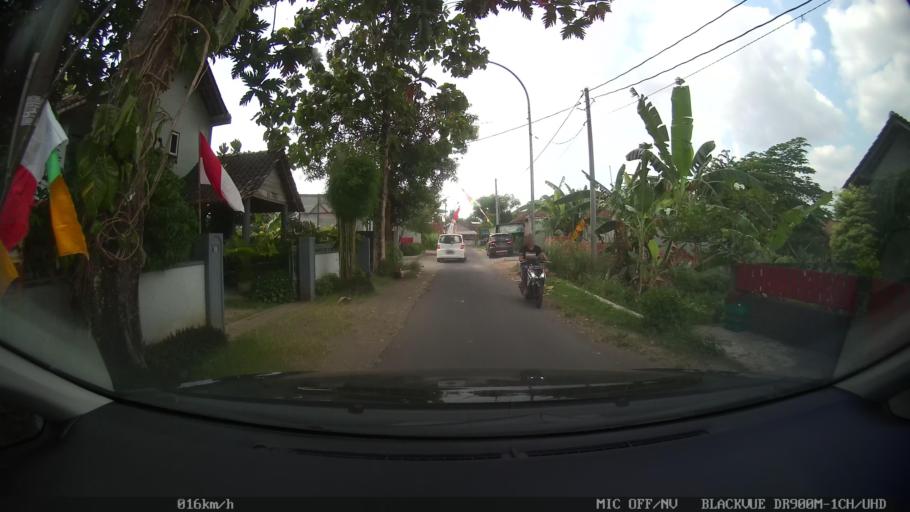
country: ID
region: Daerah Istimewa Yogyakarta
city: Kasihan
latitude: -7.8208
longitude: 110.3394
